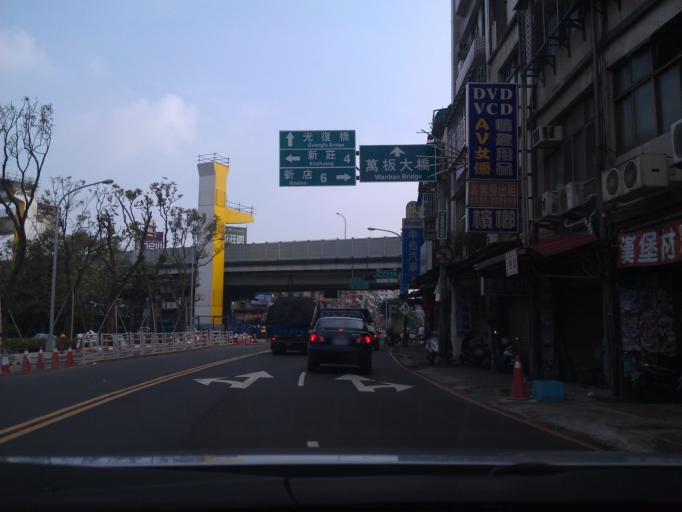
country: TW
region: Taipei
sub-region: Taipei
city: Banqiao
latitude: 25.0102
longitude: 121.4788
